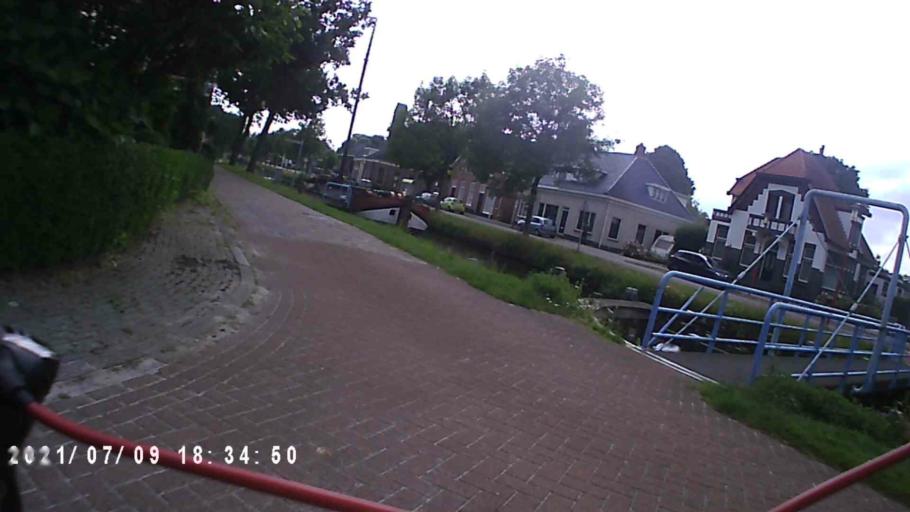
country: NL
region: Groningen
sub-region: Gemeente Pekela
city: Oude Pekela
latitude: 53.0745
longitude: 6.9632
